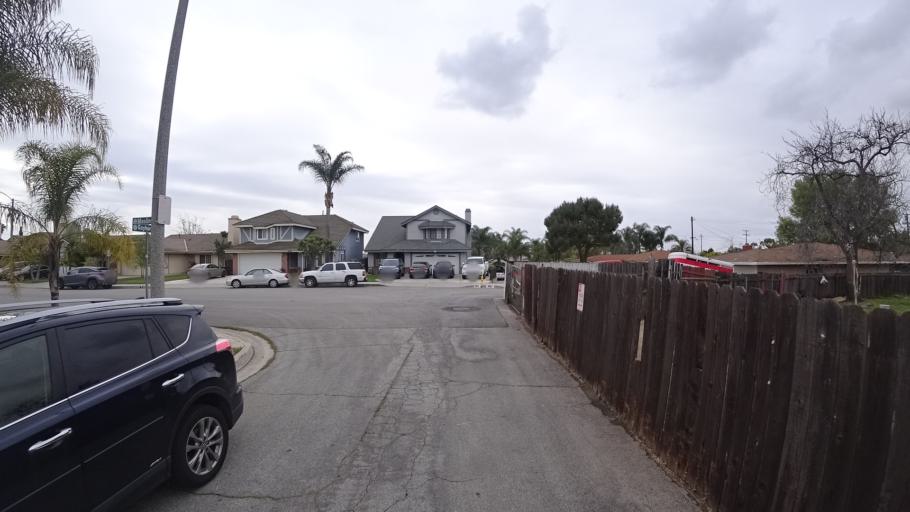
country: US
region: California
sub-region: Los Angeles County
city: Irwindale
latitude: 34.1009
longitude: -117.9495
